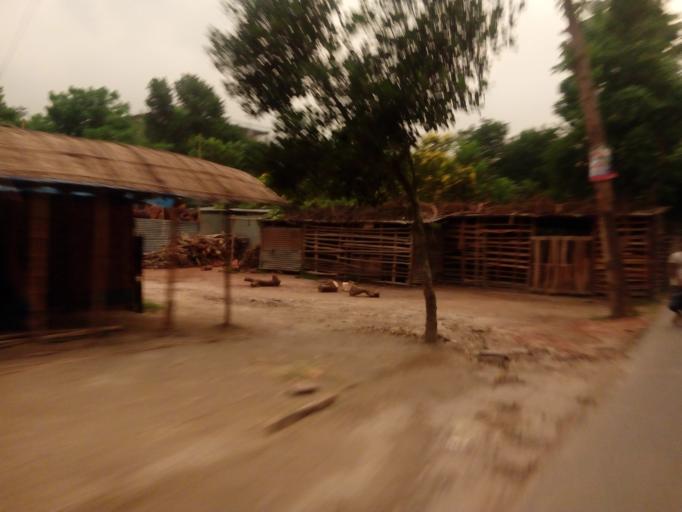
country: BD
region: Rajshahi
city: Sirajganj
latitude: 24.3030
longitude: 89.6970
